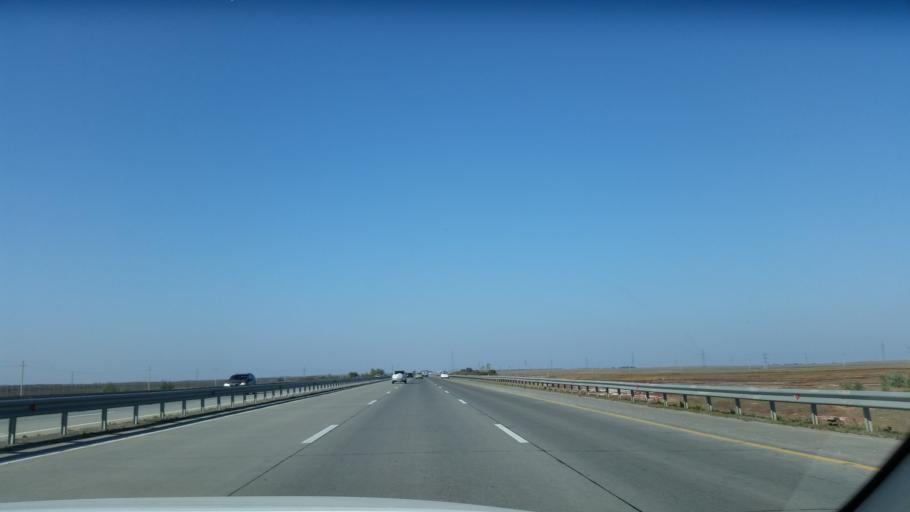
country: KZ
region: Astana Qalasy
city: Astana
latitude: 51.2740
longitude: 71.3662
